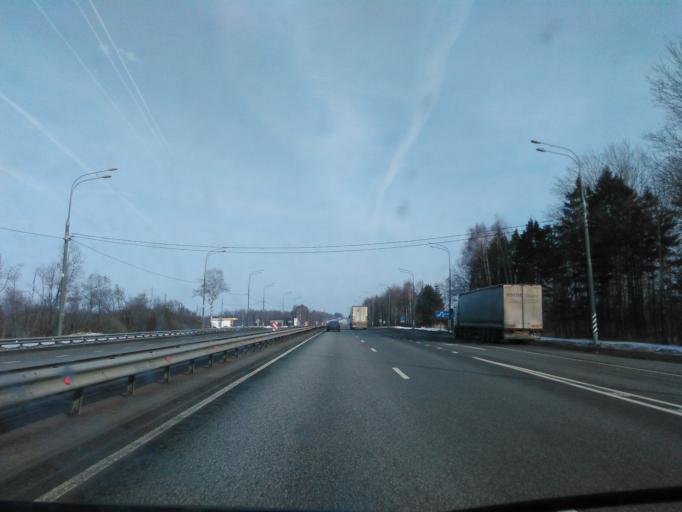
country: RU
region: Smolensk
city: Safonovo
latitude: 55.1278
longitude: 33.1479
